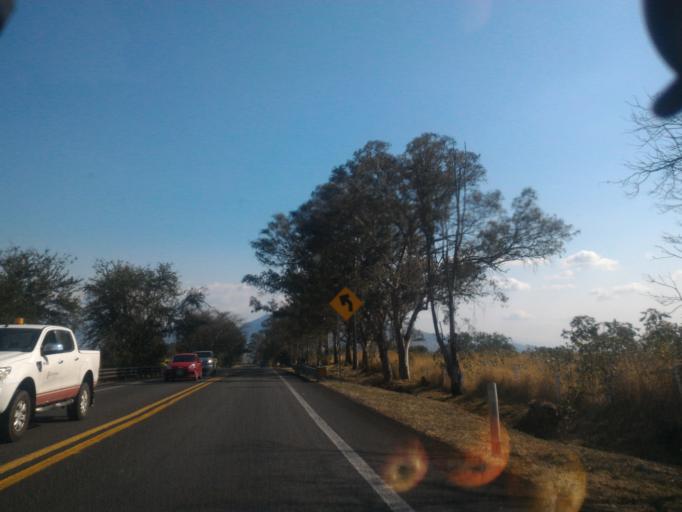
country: MX
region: Jalisco
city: Tuxpan
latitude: 19.5599
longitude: -103.4404
